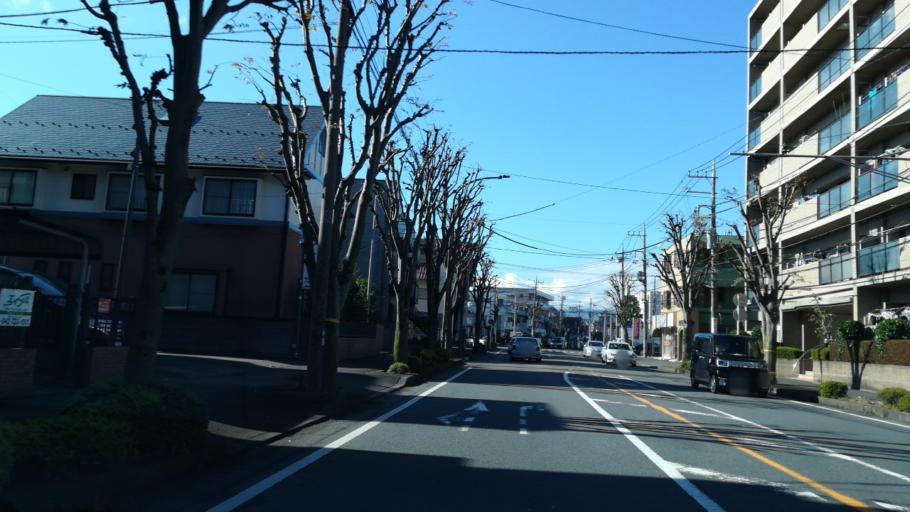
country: JP
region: Tokyo
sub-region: Machida-shi
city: Machida
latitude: 35.5661
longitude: 139.3852
